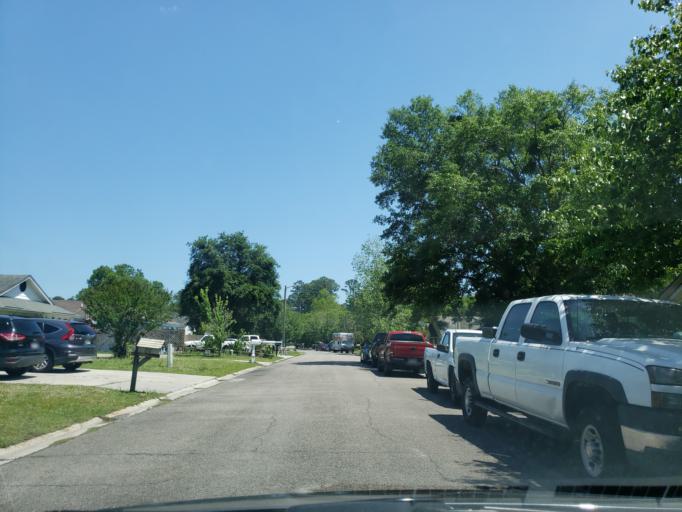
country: US
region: Georgia
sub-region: Chatham County
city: Isle of Hope
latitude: 31.9814
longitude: -81.0810
